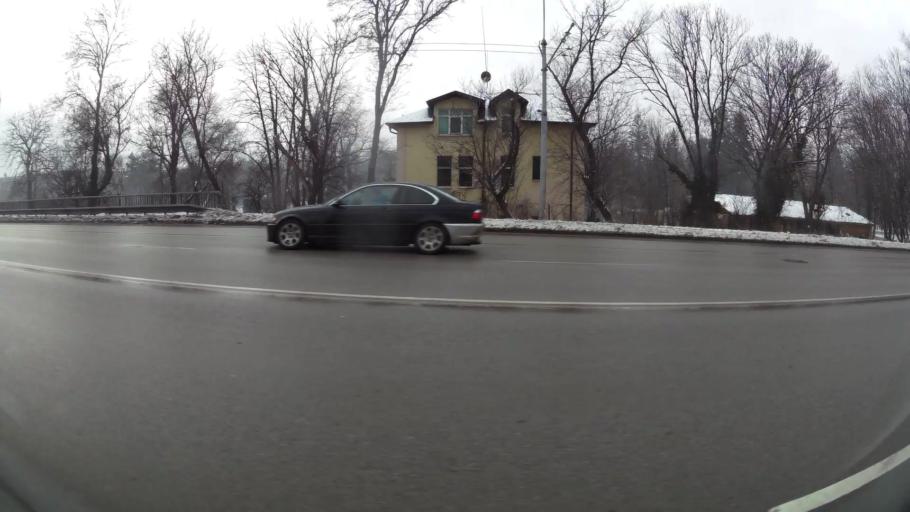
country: BG
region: Sofia-Capital
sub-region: Stolichna Obshtina
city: Sofia
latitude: 42.7136
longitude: 23.2865
